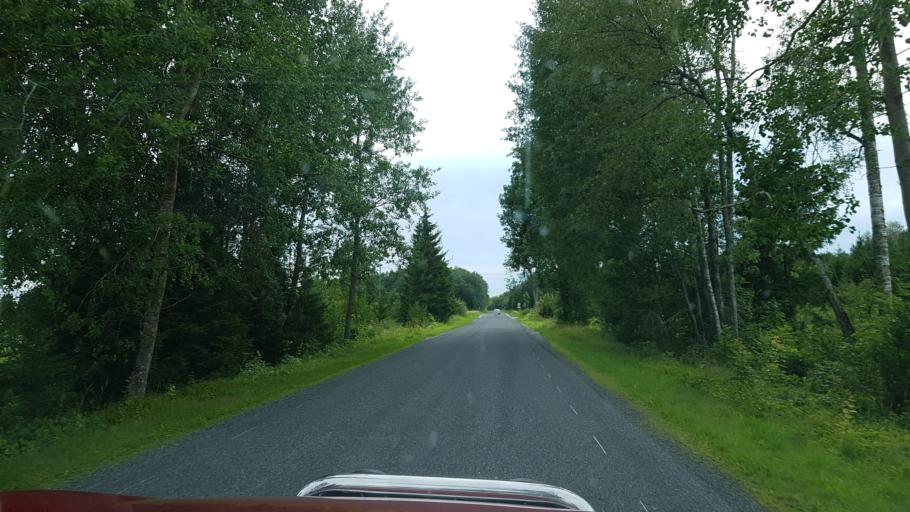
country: EE
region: Laeaene
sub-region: Lihula vald
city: Lihula
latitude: 58.8900
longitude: 23.8777
